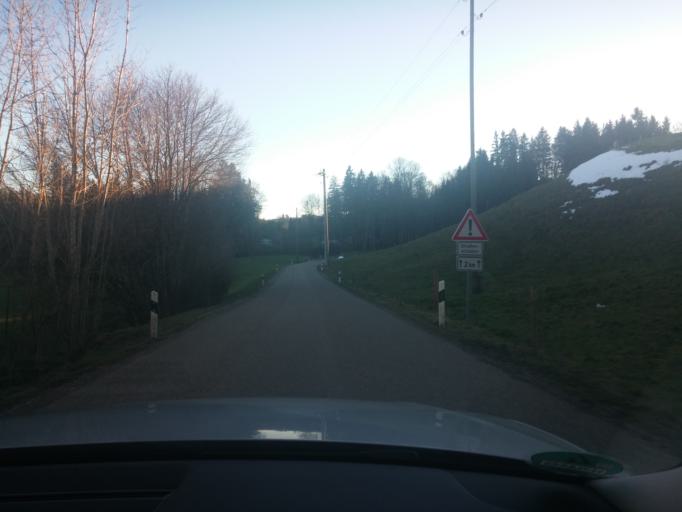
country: DE
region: Bavaria
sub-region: Swabia
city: Altusried
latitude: 47.8279
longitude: 10.1759
